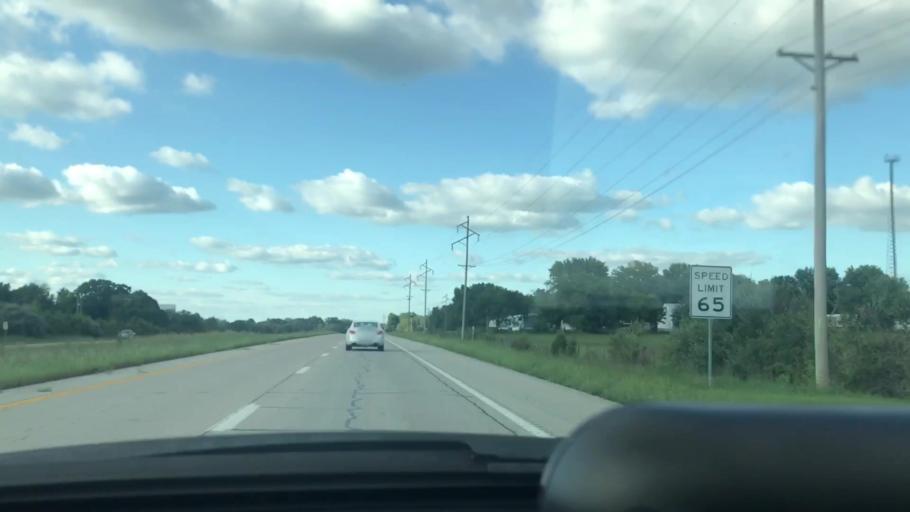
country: US
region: Missouri
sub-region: Pettis County
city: Sedalia
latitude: 38.6274
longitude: -93.2672
